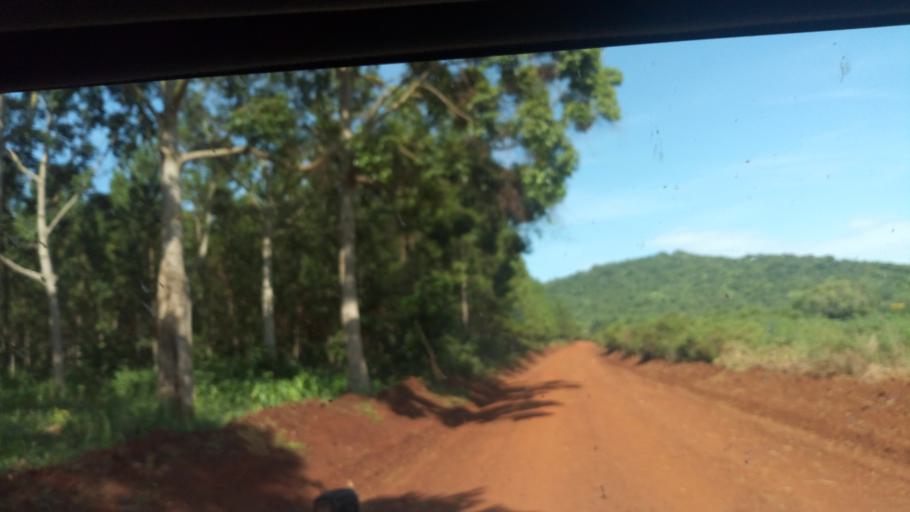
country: UG
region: Western Region
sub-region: Masindi District
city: Masindi
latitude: 1.6510
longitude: 31.7815
